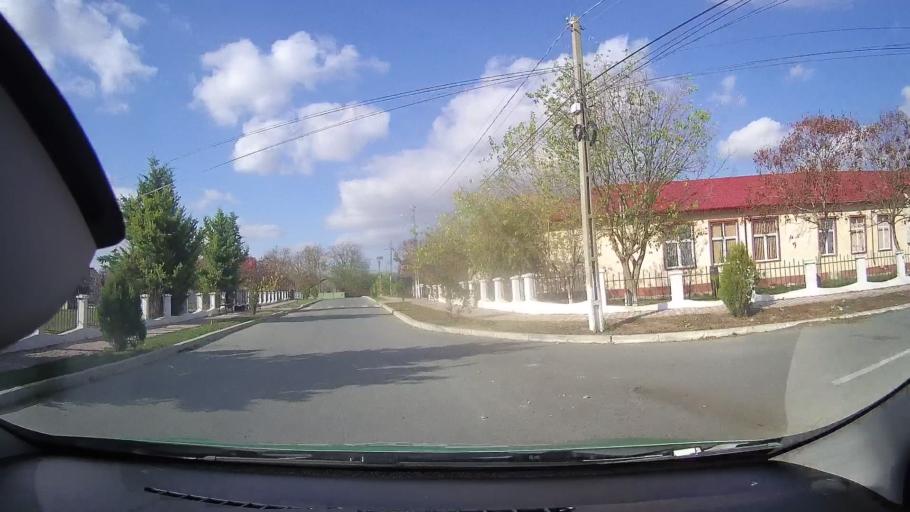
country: RO
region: Constanta
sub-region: Comuna Istria
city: Istria
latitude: 44.5724
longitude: 28.7120
